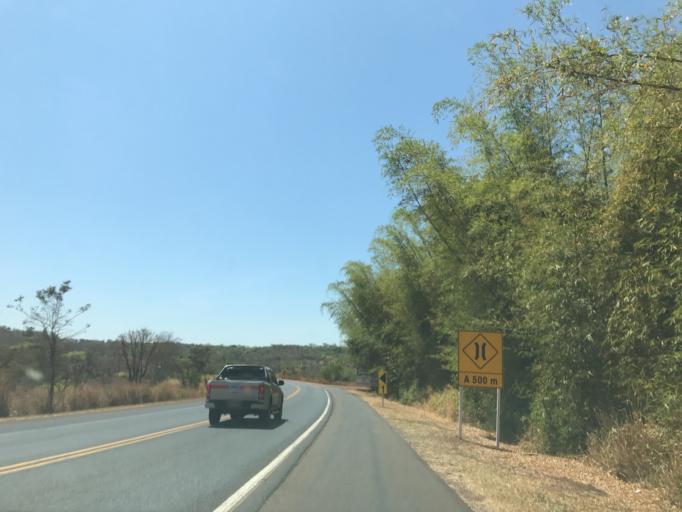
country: BR
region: Minas Gerais
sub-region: Prata
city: Prata
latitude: -19.3520
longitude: -48.8976
